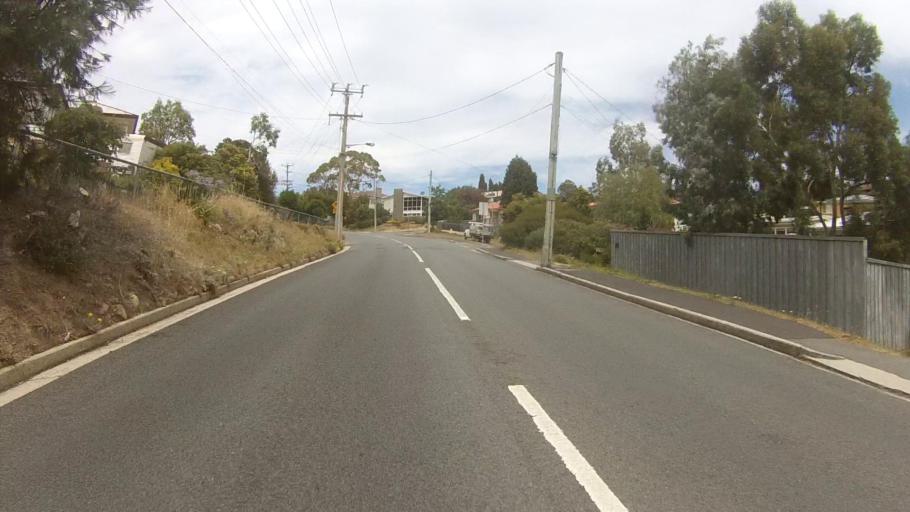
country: AU
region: Tasmania
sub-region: Clarence
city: Lindisfarne
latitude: -42.8543
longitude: 147.3711
